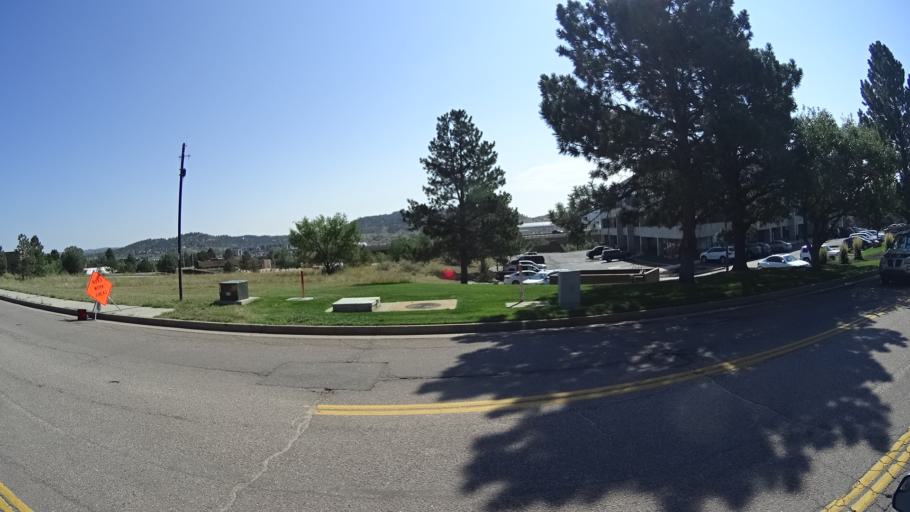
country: US
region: Colorado
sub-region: El Paso County
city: Colorado Springs
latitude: 38.9113
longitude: -104.8258
